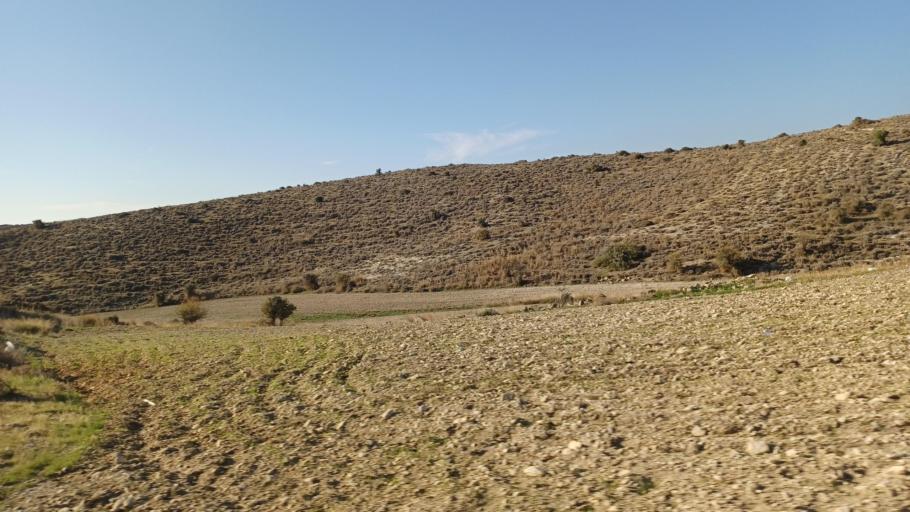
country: CY
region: Larnaka
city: Psevdas
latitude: 34.9397
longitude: 33.5227
